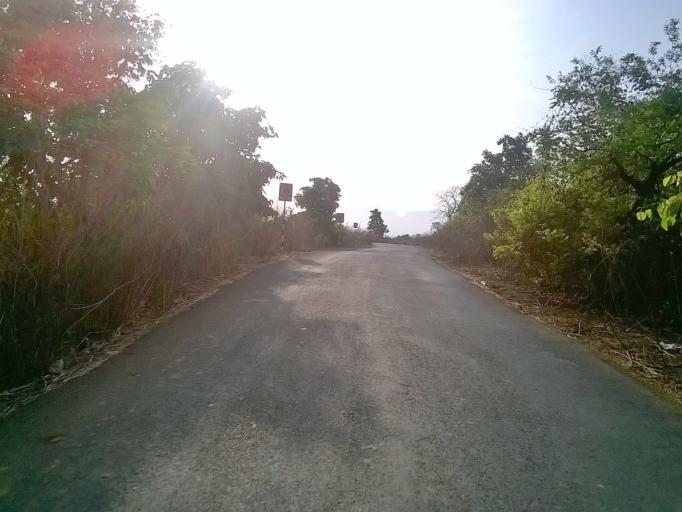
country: IN
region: Maharashtra
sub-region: Raigarh
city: Matheran
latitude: 19.0267
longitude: 73.2227
